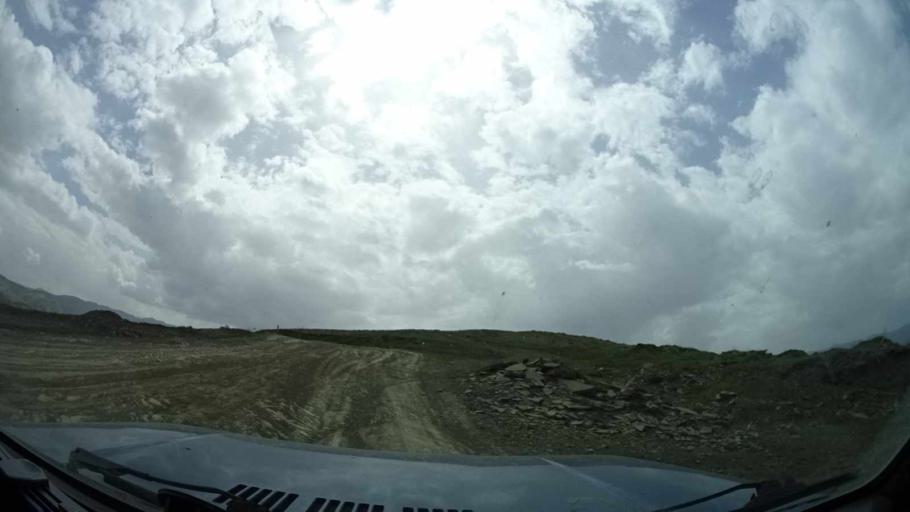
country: RU
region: Dagestan
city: Kubachi
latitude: 42.0852
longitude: 47.5625
